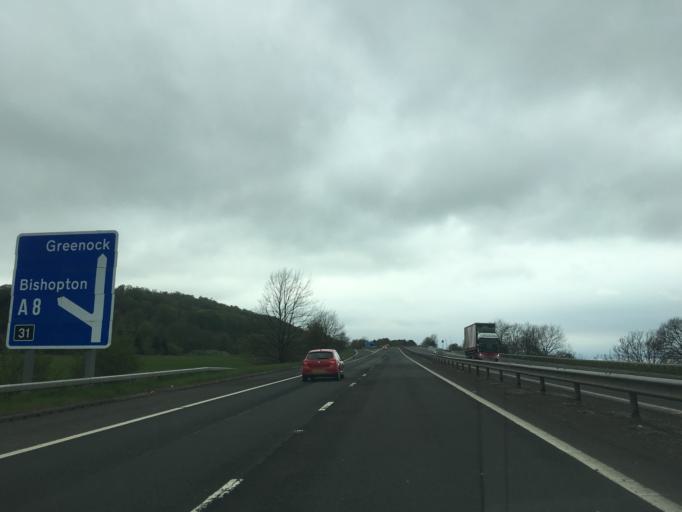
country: GB
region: Scotland
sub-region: West Dunbartonshire
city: Dumbarton
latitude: 55.9233
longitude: -4.5480
